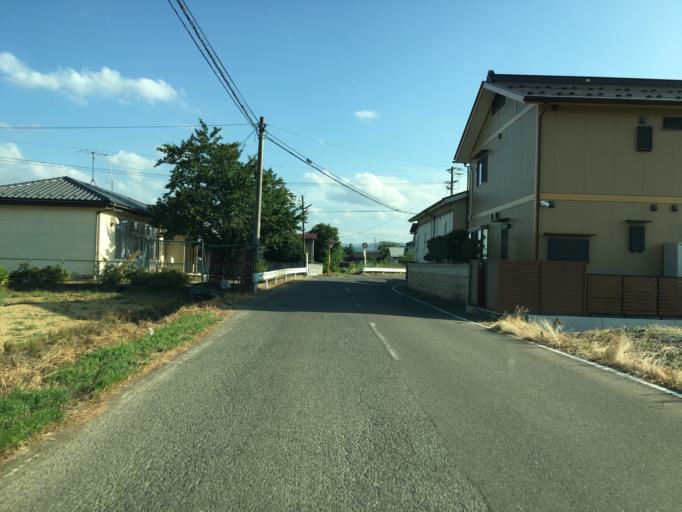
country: JP
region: Fukushima
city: Yanagawamachi-saiwaicho
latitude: 37.8355
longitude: 140.5846
